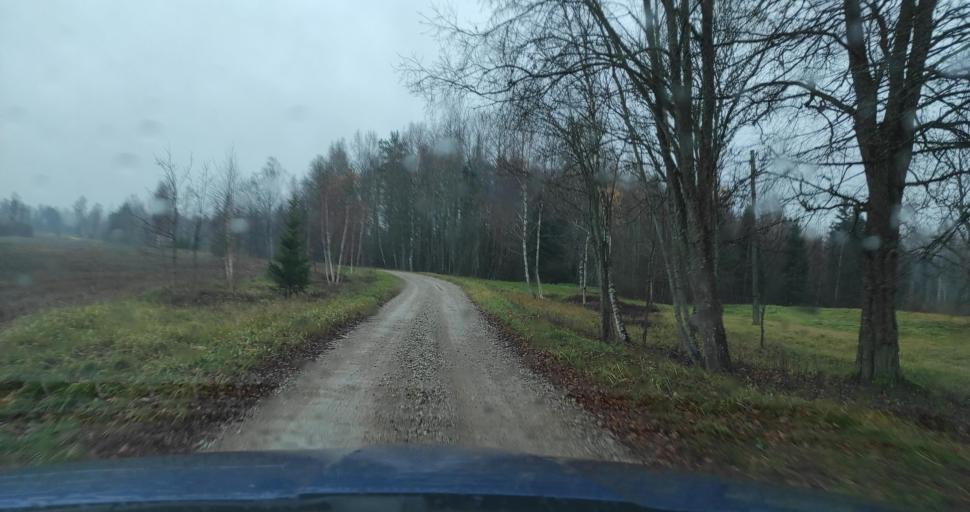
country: LV
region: Alsunga
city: Alsunga
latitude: 56.8887
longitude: 21.5904
